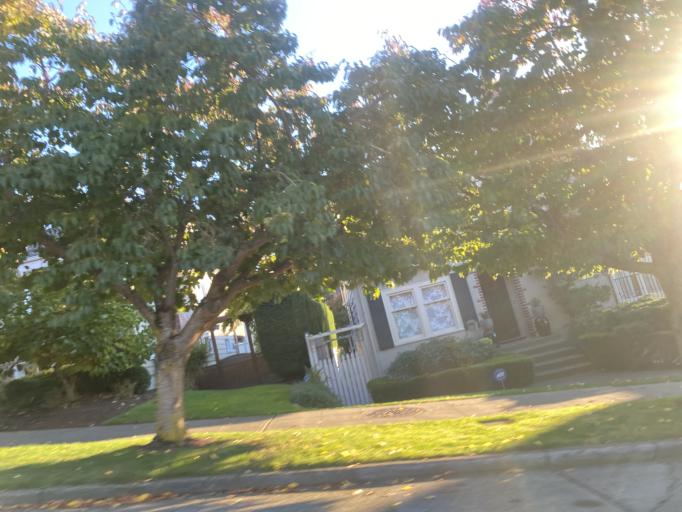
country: US
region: Washington
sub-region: King County
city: Seattle
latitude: 47.6396
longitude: -122.3949
